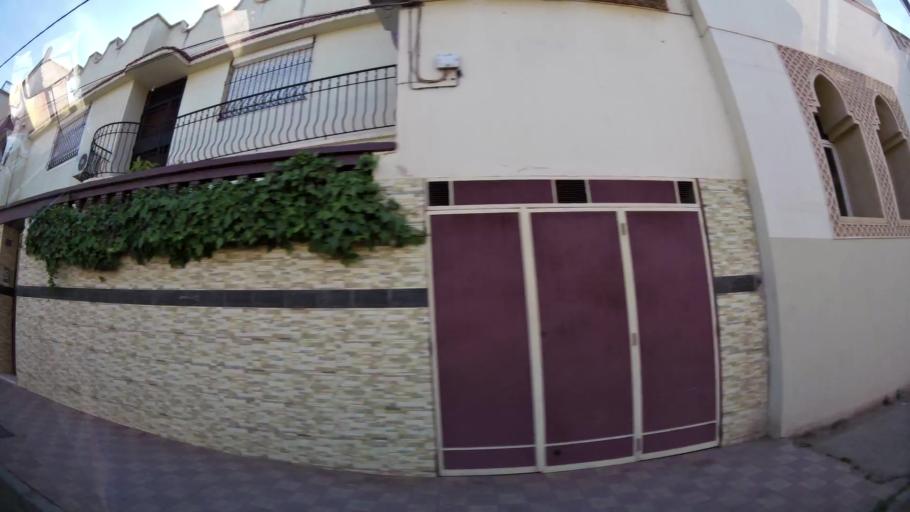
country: MA
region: Oriental
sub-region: Oujda-Angad
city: Oujda
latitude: 34.6736
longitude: -1.9082
